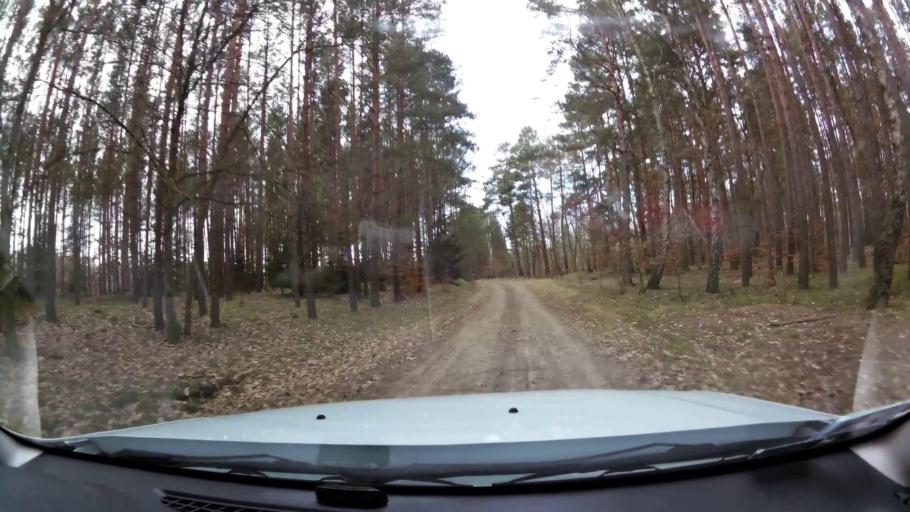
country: PL
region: West Pomeranian Voivodeship
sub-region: Powiat drawski
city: Drawsko Pomorskie
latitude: 53.5348
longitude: 15.6975
